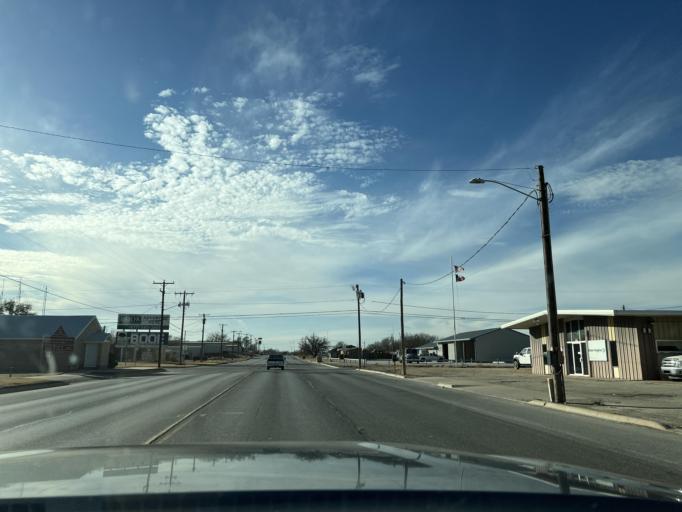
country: US
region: Texas
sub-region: Scurry County
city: Snyder
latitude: 32.7173
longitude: -100.9263
